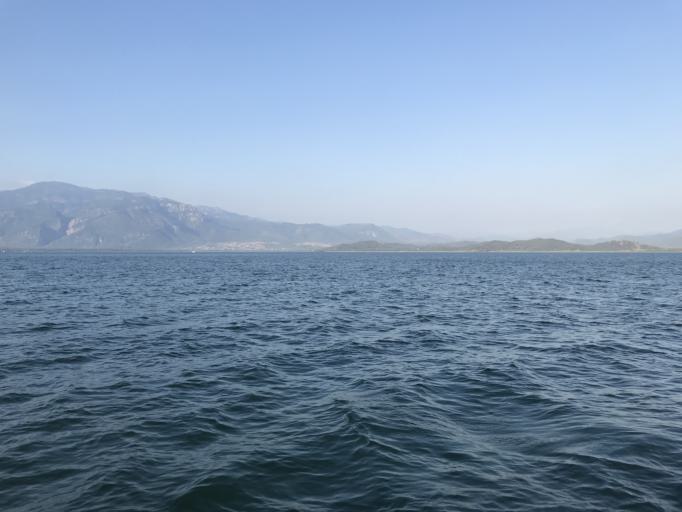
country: TR
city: Dalyan
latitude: 36.9191
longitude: 28.6499
